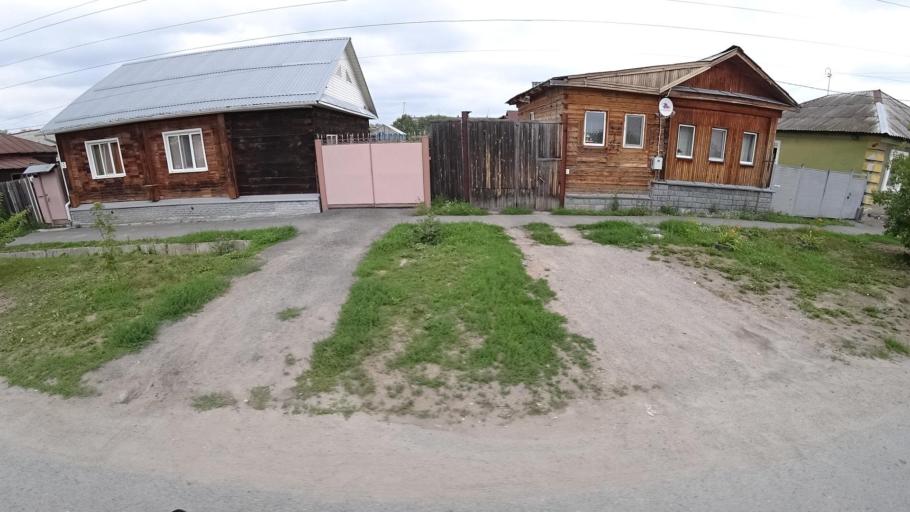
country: RU
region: Sverdlovsk
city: Kamyshlov
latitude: 56.8419
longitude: 62.7037
